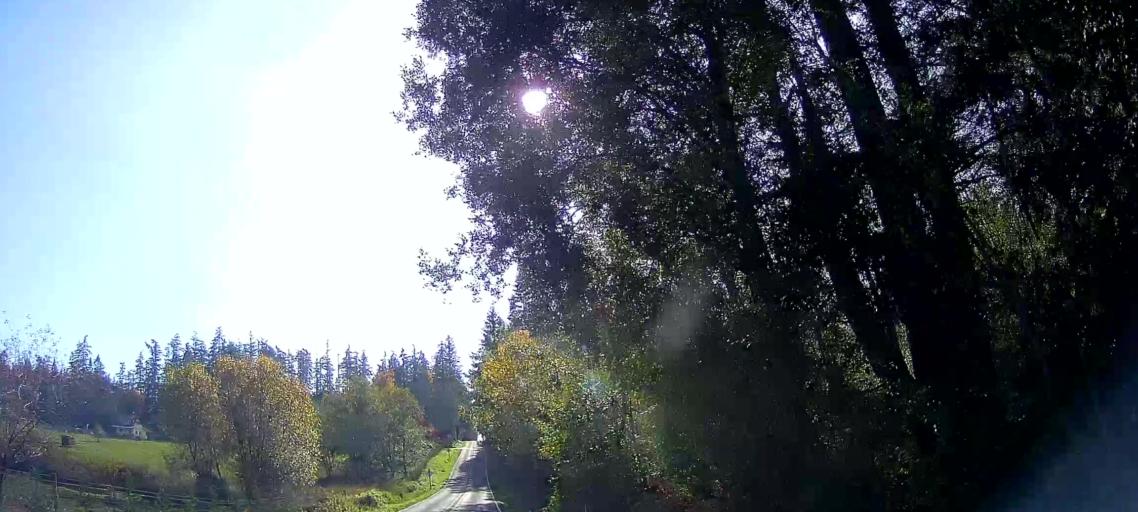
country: US
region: Washington
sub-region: Island County
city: Camano
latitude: 48.2164
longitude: -122.4560
